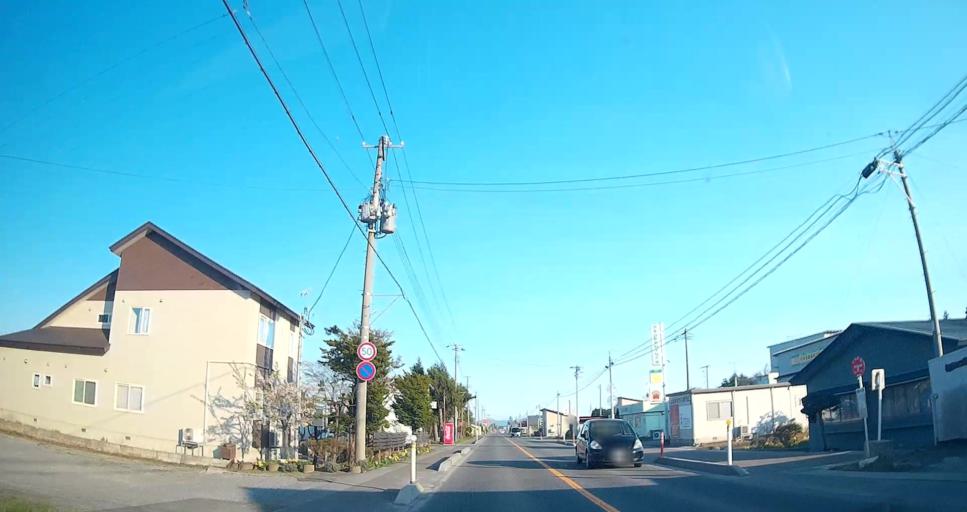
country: JP
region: Aomori
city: Mutsu
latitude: 41.2690
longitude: 141.2196
